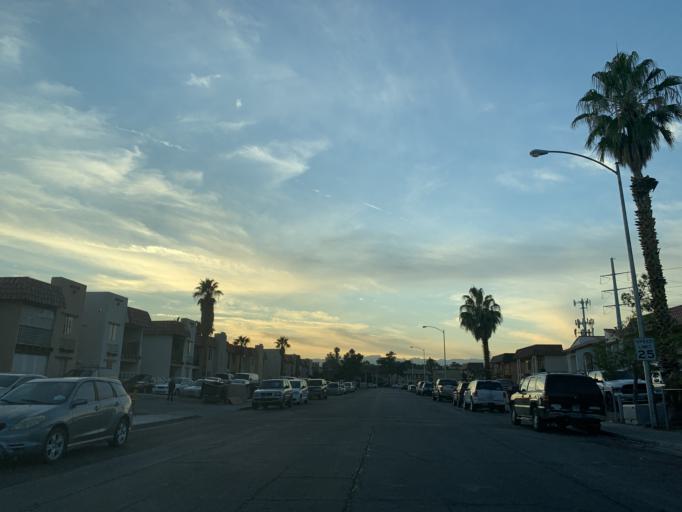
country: US
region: Nevada
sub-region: Clark County
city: Spring Valley
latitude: 36.1127
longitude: -115.2126
